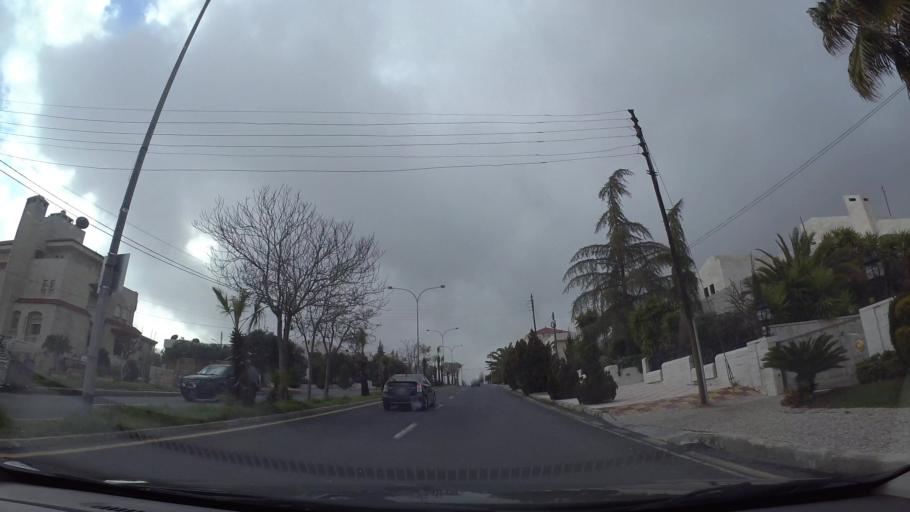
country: JO
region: Amman
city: Al Bunayyat ash Shamaliyah
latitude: 31.9515
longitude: 35.8849
